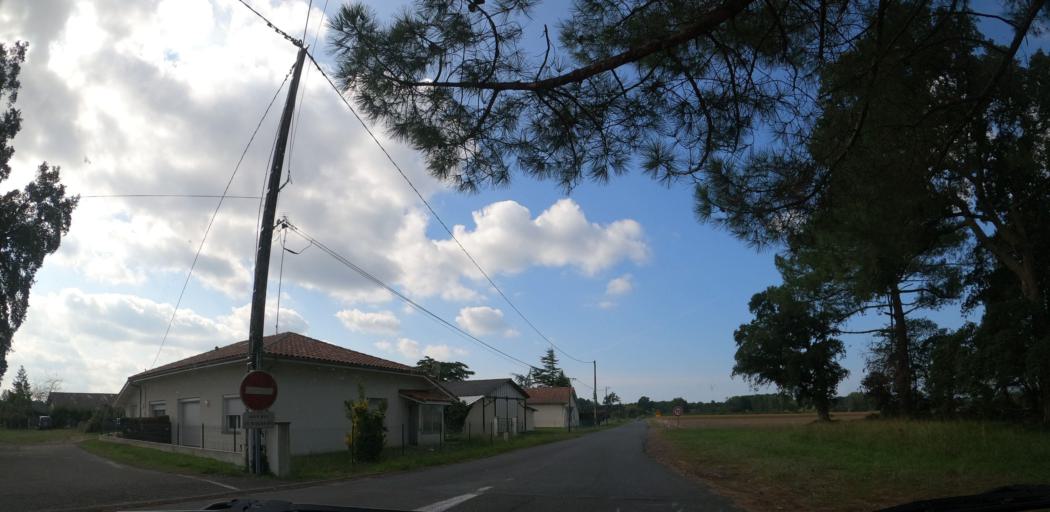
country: FR
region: Aquitaine
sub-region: Departement des Landes
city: Tosse
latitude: 43.7175
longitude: -1.3466
